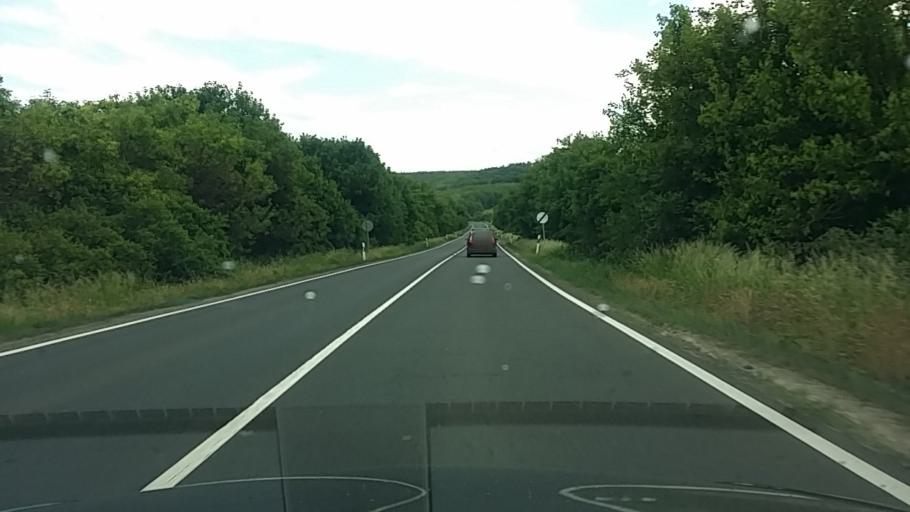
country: HU
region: Nograd
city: Retsag
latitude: 47.9691
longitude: 19.1278
